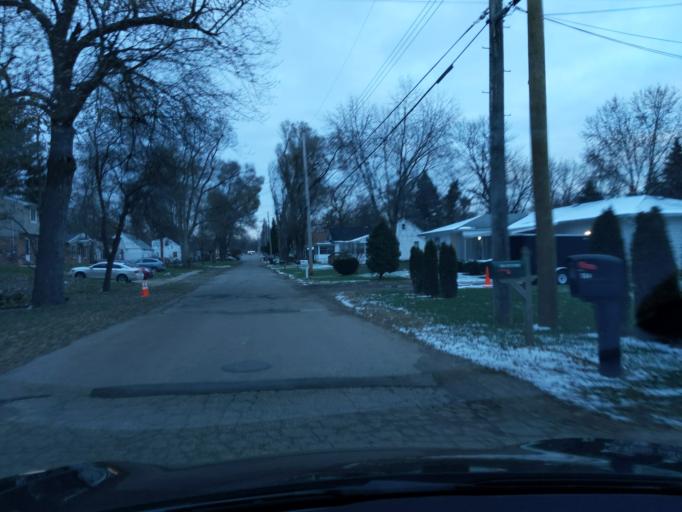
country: US
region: Michigan
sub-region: Ingham County
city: Lansing
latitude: 42.7656
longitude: -84.5456
